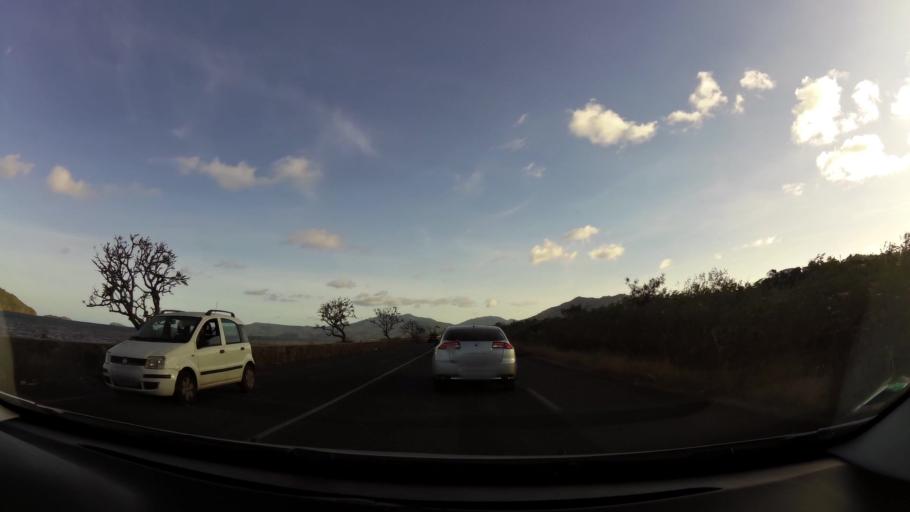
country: YT
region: Mamoudzou
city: Mamoudzou
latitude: -12.7898
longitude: 45.2237
